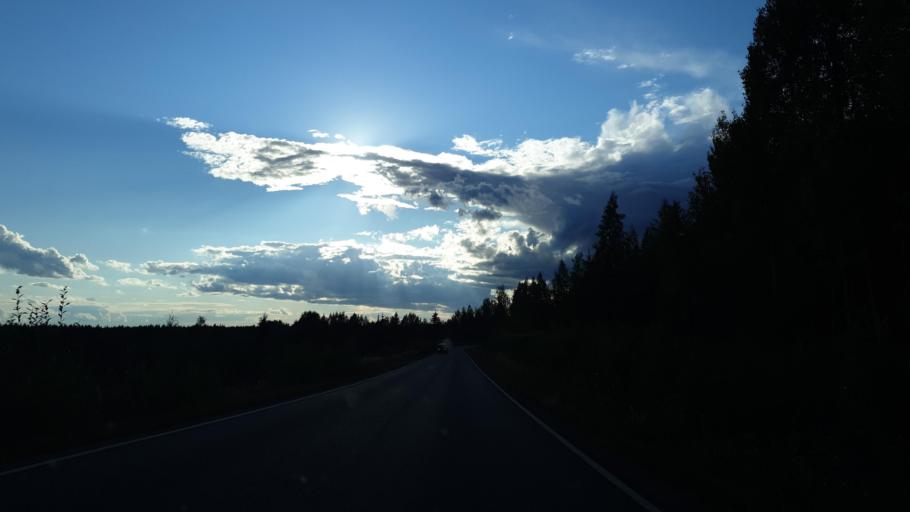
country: FI
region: Northern Savo
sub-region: Koillis-Savo
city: Juankoski
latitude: 63.1722
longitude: 28.3719
